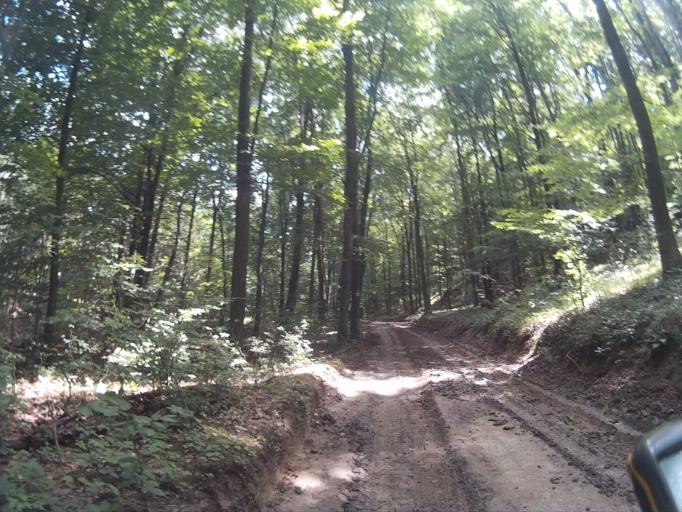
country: HU
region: Veszprem
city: Zirc
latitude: 47.2017
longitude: 17.9085
